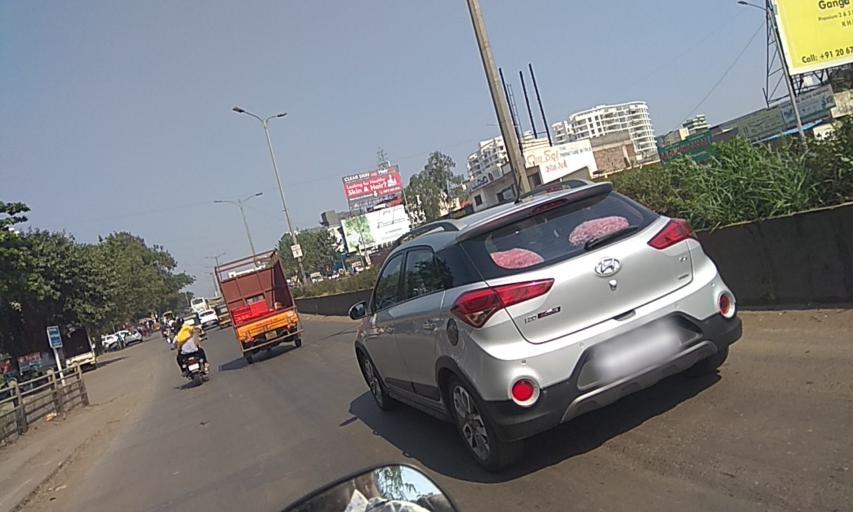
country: IN
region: Maharashtra
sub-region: Pune Division
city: Lohogaon
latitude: 18.5374
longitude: 73.9341
